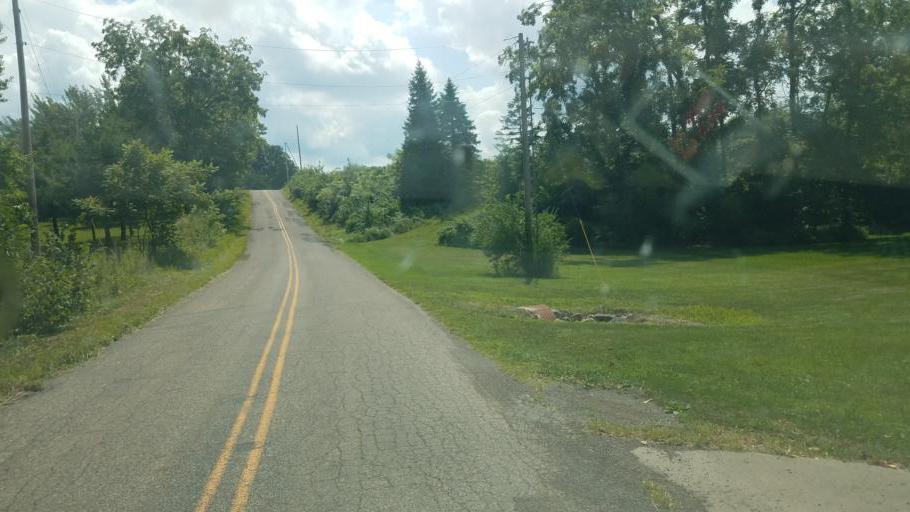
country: US
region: Ohio
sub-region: Knox County
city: Mount Vernon
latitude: 40.3849
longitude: -82.5825
